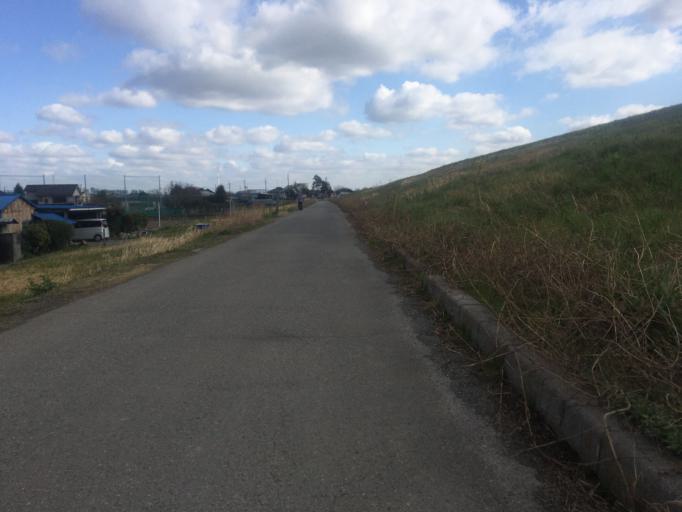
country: JP
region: Saitama
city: Shiki
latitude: 35.8665
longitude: 139.5912
